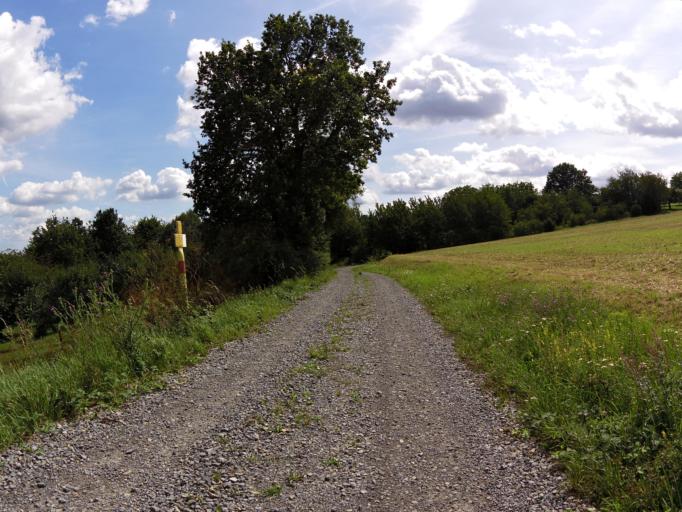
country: DE
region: Bavaria
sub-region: Regierungsbezirk Unterfranken
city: Margetshochheim
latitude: 49.8399
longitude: 9.8477
